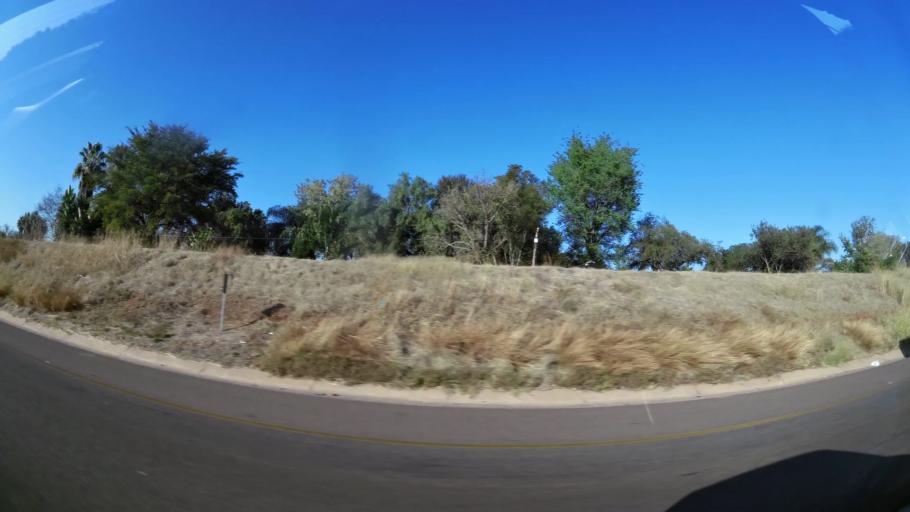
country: ZA
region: Gauteng
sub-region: City of Tshwane Metropolitan Municipality
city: Pretoria
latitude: -25.6426
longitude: 28.2352
